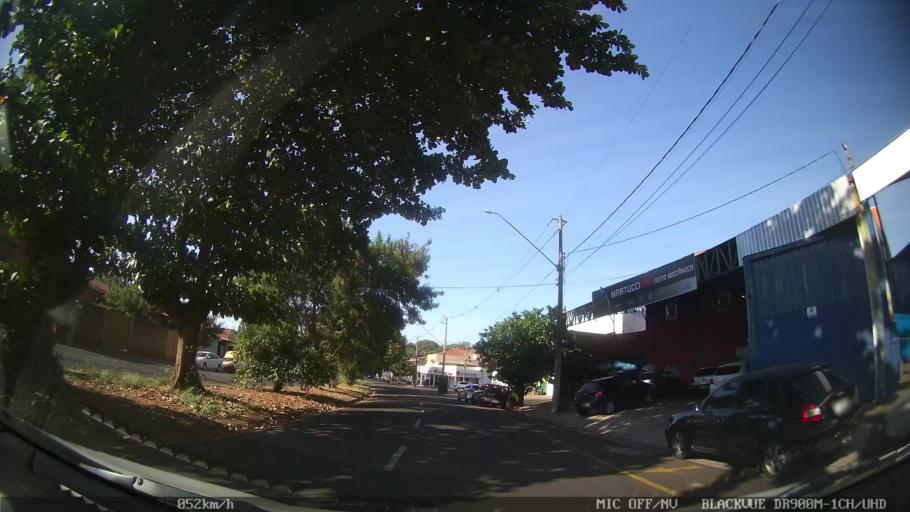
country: BR
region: Sao Paulo
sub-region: Sao Jose Do Rio Preto
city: Sao Jose do Rio Preto
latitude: -20.7792
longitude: -49.3581
